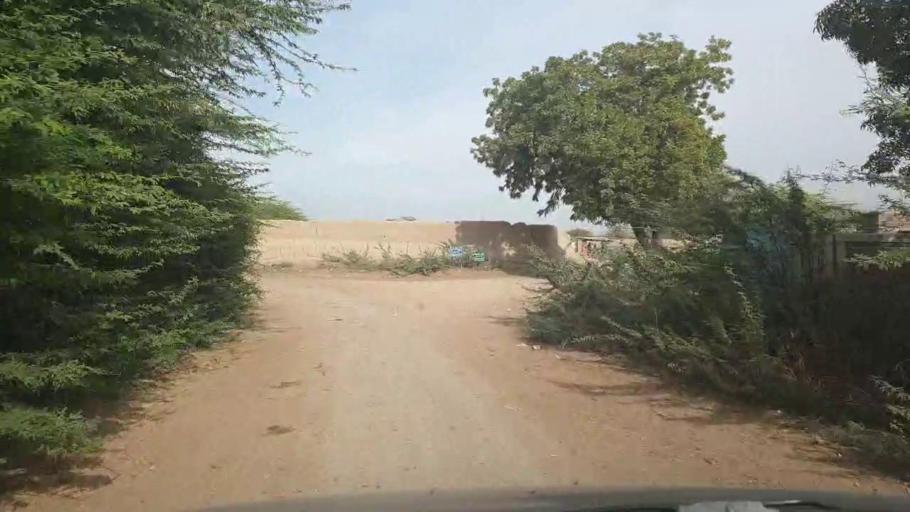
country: PK
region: Sindh
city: Kunri
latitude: 25.2935
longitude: 69.5877
